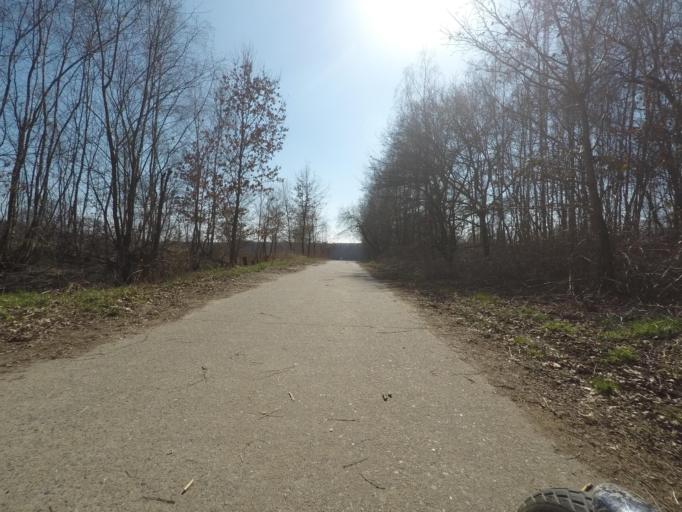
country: DE
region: Schleswig-Holstein
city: Stapelfeld
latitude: 53.6274
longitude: 10.1970
